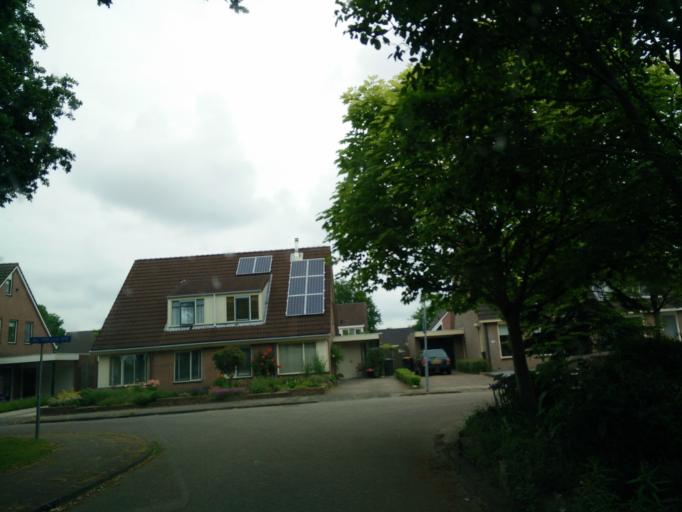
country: NL
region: Drenthe
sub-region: Gemeente Assen
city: Assen
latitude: 53.0224
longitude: 6.5879
